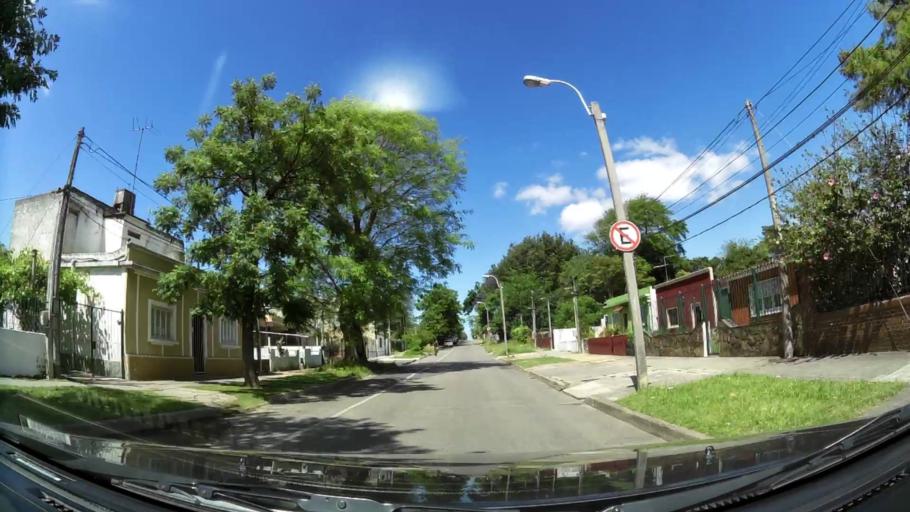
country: UY
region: Montevideo
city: Montevideo
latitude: -34.8542
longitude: -56.1347
